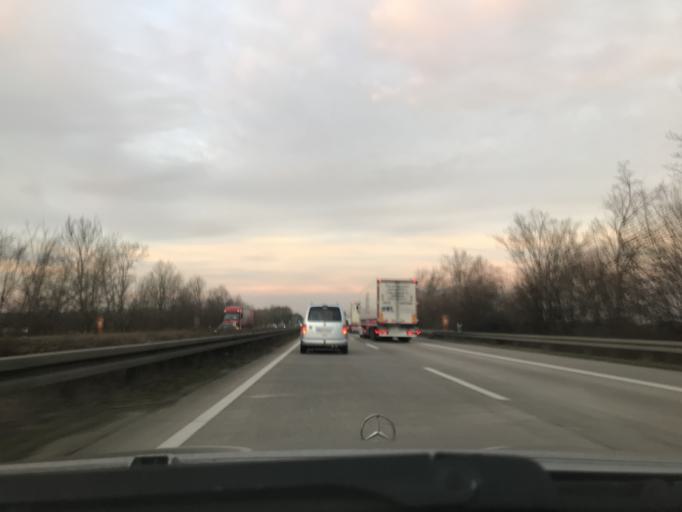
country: DE
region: North Rhine-Westphalia
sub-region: Regierungsbezirk Arnsberg
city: Anrochte
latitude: 51.5835
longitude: 8.3039
